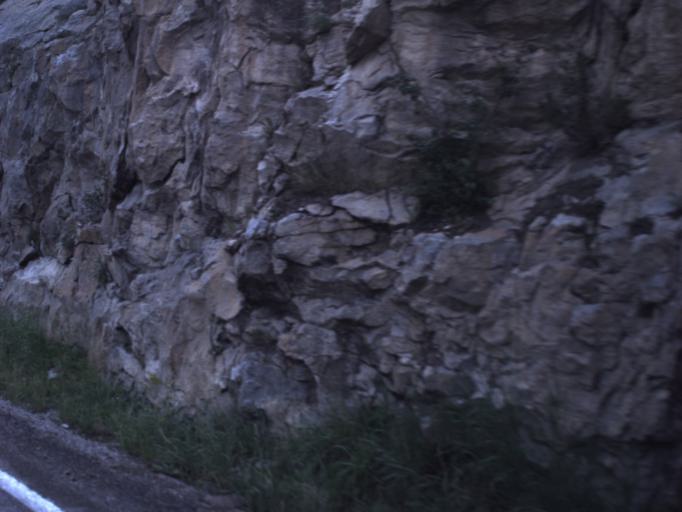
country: US
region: Utah
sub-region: Iron County
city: Cedar City
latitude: 37.6104
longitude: -112.9334
